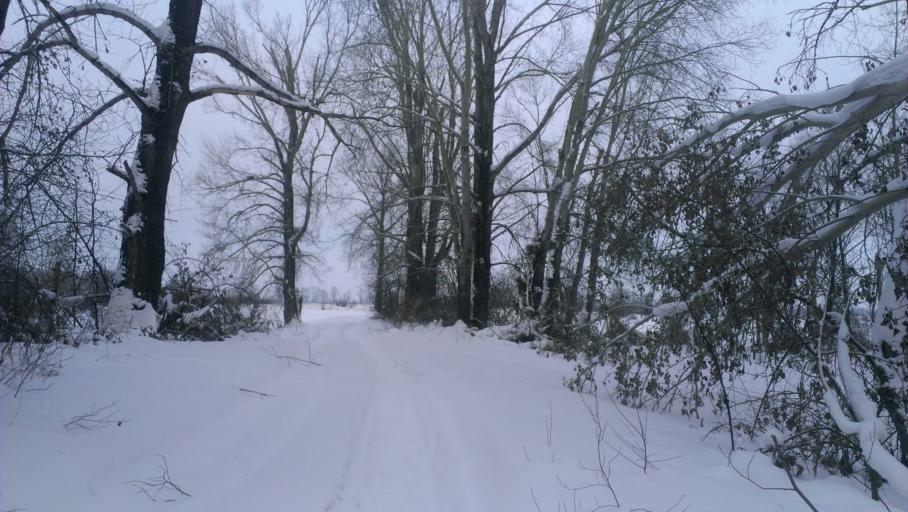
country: RU
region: Altai Krai
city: Zaton
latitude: 53.3162
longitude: 83.8449
